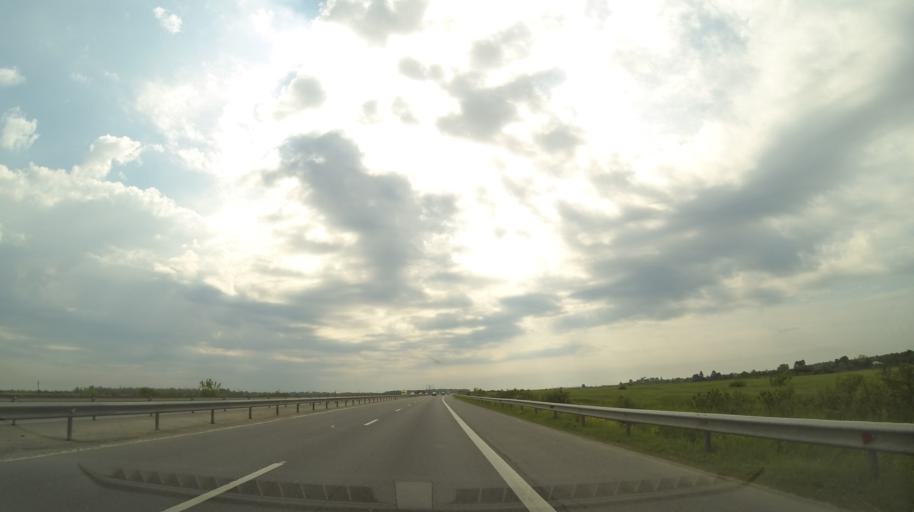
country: RO
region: Dambovita
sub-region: Comuna Mogosani
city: Zavoiu
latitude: 44.6472
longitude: 25.3810
